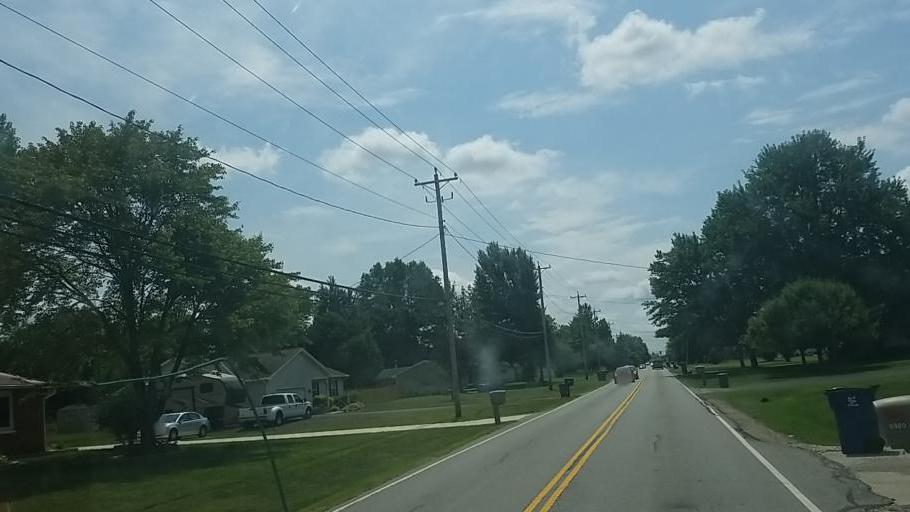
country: US
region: Ohio
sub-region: Franklin County
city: Reynoldsburg
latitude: 39.9909
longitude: -82.7674
